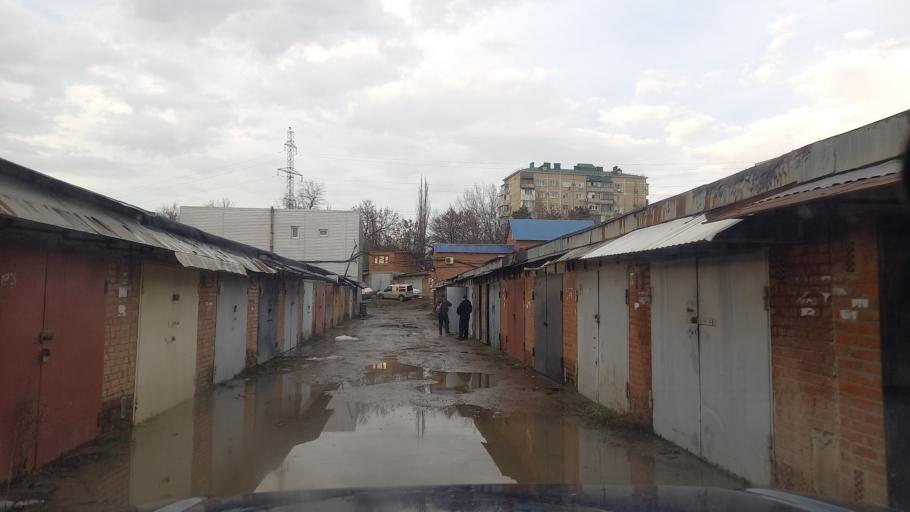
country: RU
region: Krasnodarskiy
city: Pashkovskiy
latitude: 45.0189
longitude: 39.0435
